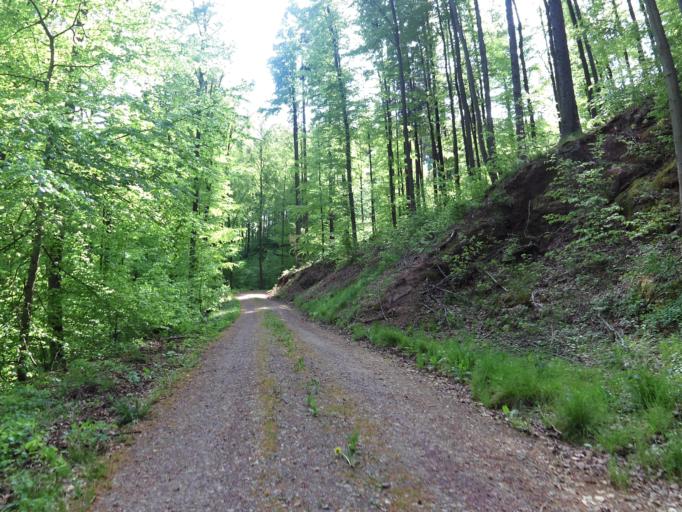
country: DE
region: Thuringia
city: Wolfsburg-Unkeroda
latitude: 50.9573
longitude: 10.2838
